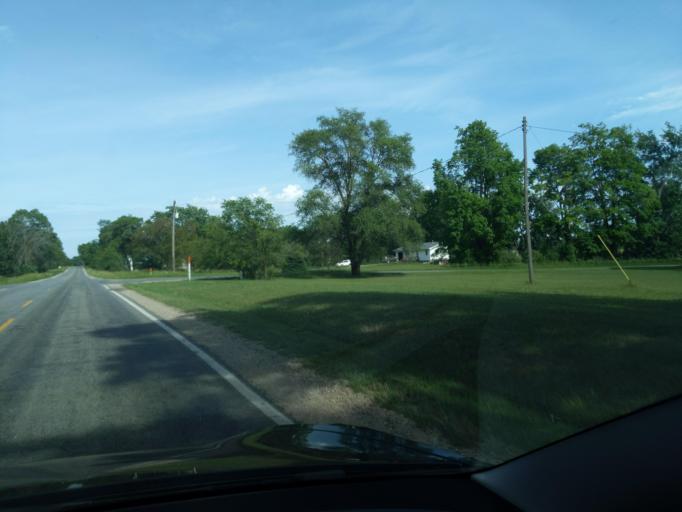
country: US
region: Michigan
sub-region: Newaygo County
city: Fremont
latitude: 43.4239
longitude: -85.9656
